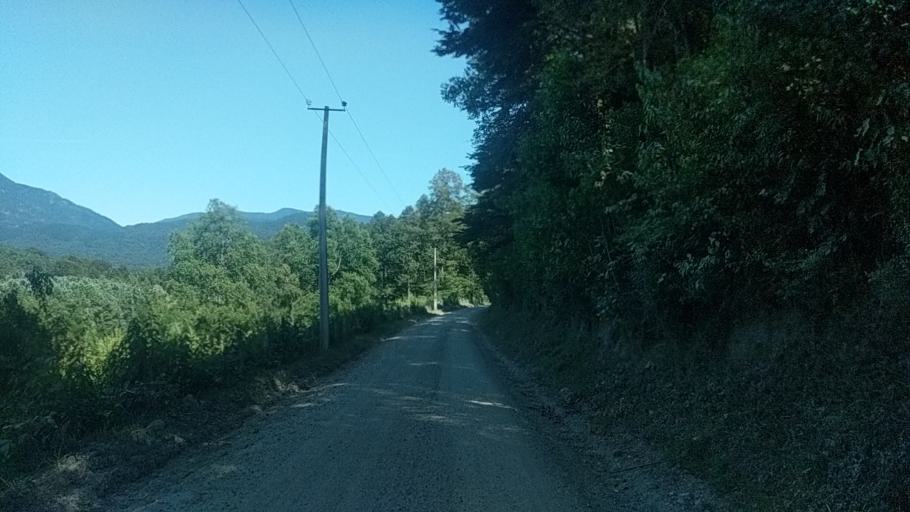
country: CL
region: Araucania
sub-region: Provincia de Cautin
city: Pucon
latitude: -39.0643
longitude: -71.7414
